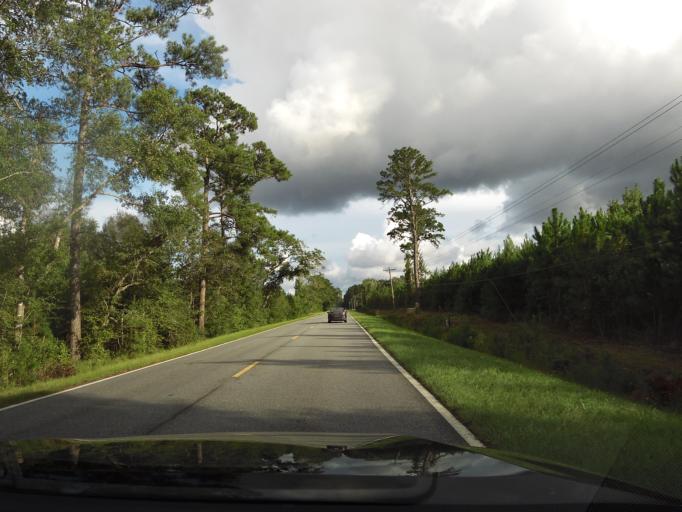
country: US
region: Georgia
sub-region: Liberty County
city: Midway
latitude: 31.8639
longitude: -81.4349
